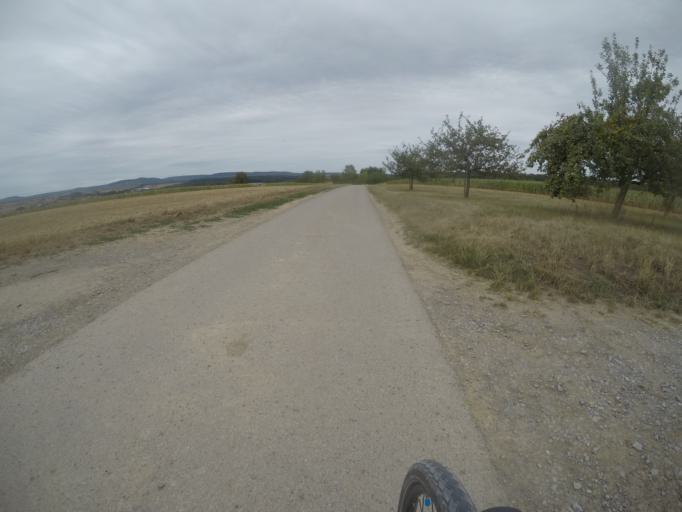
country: DE
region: Baden-Wuerttemberg
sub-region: Regierungsbezirk Stuttgart
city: Oberriexingen
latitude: 48.9187
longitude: 9.0333
